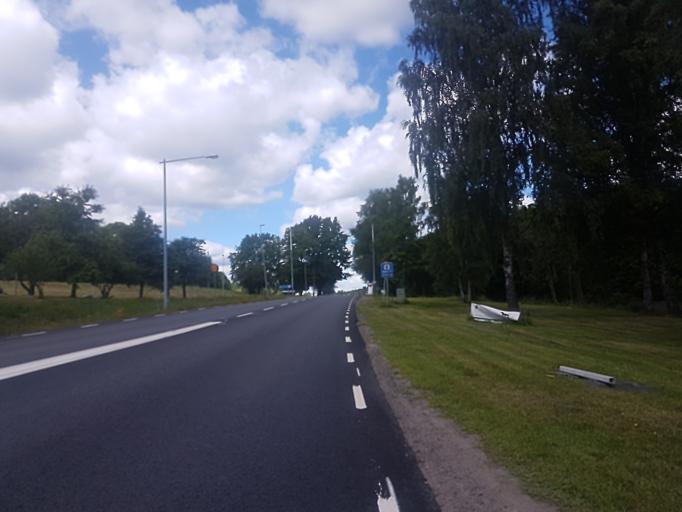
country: SE
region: Soedermanland
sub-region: Gnesta Kommun
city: Gnesta
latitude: 59.0345
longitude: 17.3317
